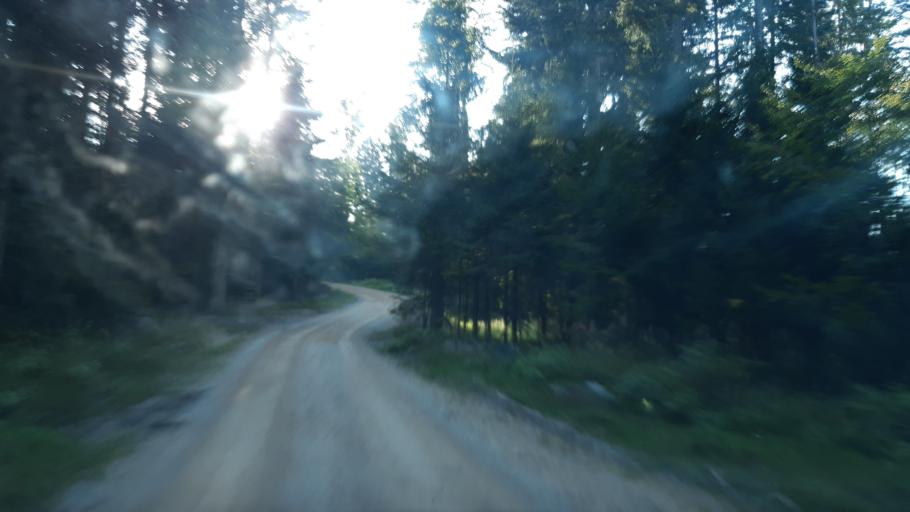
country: SI
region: Dolenjske Toplice
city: Dolenjske Toplice
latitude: 45.6952
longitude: 15.0121
